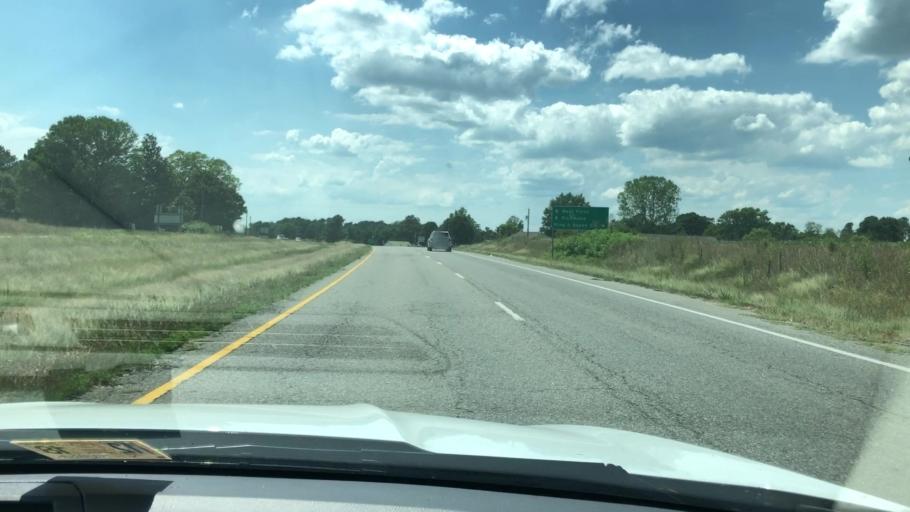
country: US
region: Virginia
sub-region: King William County
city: West Point
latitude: 37.5488
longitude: -76.7315
